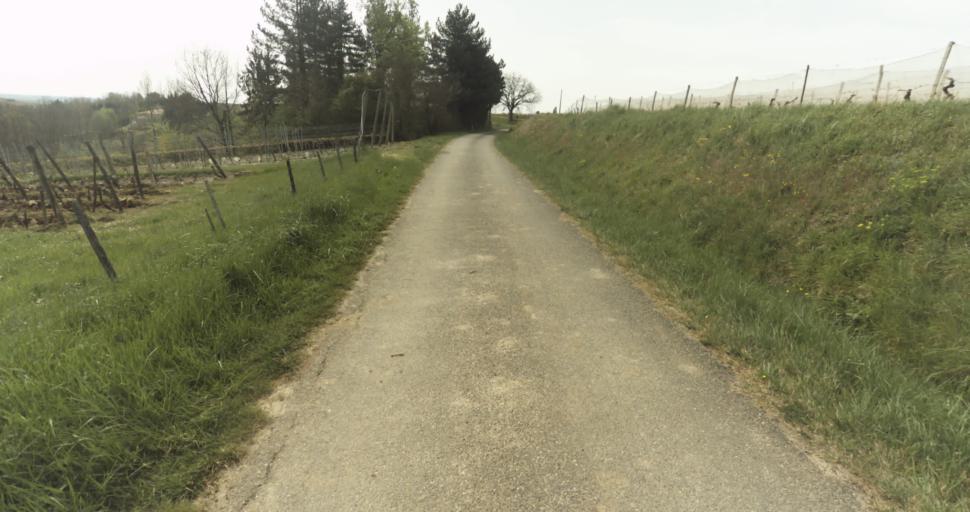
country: FR
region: Midi-Pyrenees
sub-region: Departement du Tarn-et-Garonne
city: Moissac
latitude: 44.1168
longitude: 1.0548
